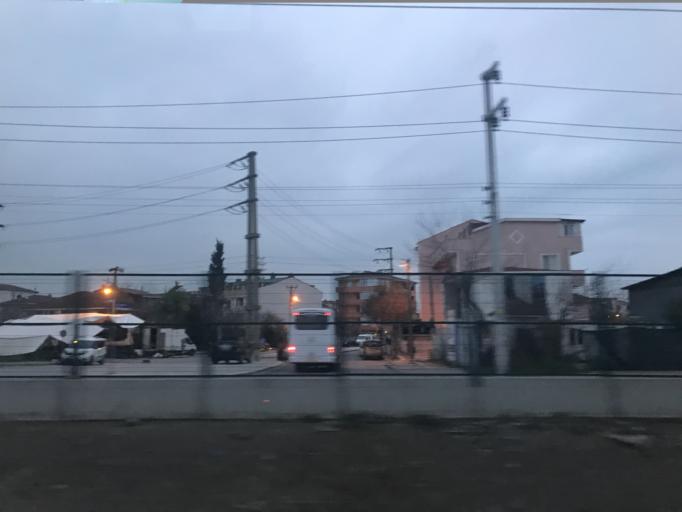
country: TR
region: Kocaeli
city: Darica
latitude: 40.7903
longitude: 29.3932
